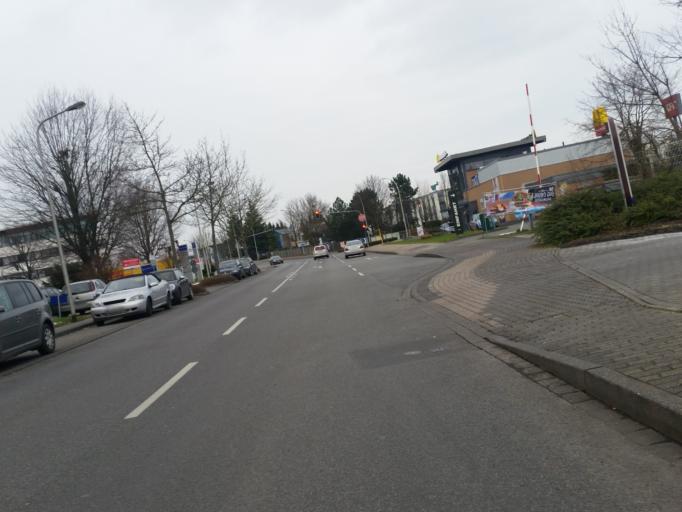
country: DE
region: North Rhine-Westphalia
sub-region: Regierungsbezirk Koln
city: Wurselen
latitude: 50.8044
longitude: 6.1535
